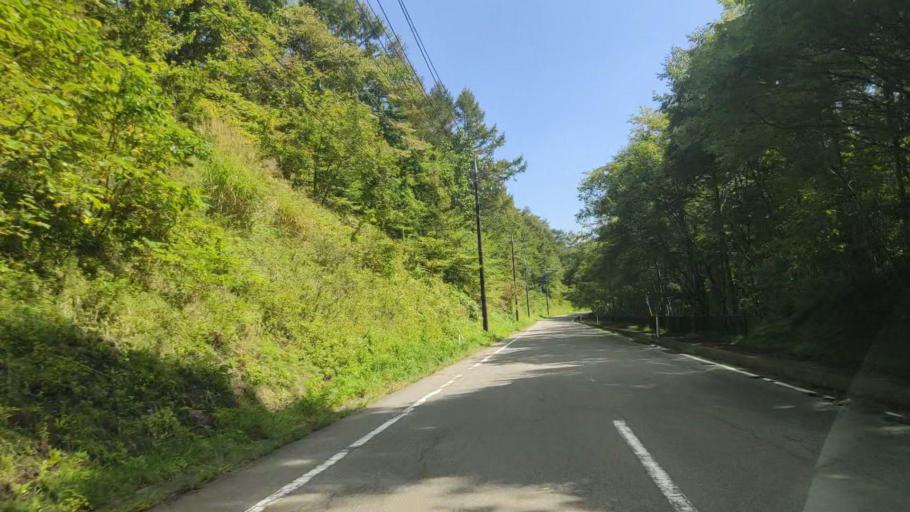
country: JP
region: Gunma
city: Nakanojomachi
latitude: 36.6399
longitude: 138.6059
